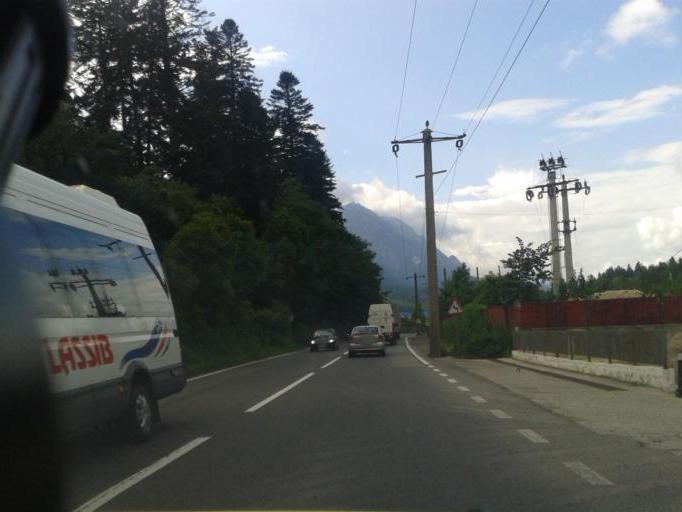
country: RO
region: Prahova
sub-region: Oras Sinaia
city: Sinaia
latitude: 45.3609
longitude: 25.5502
